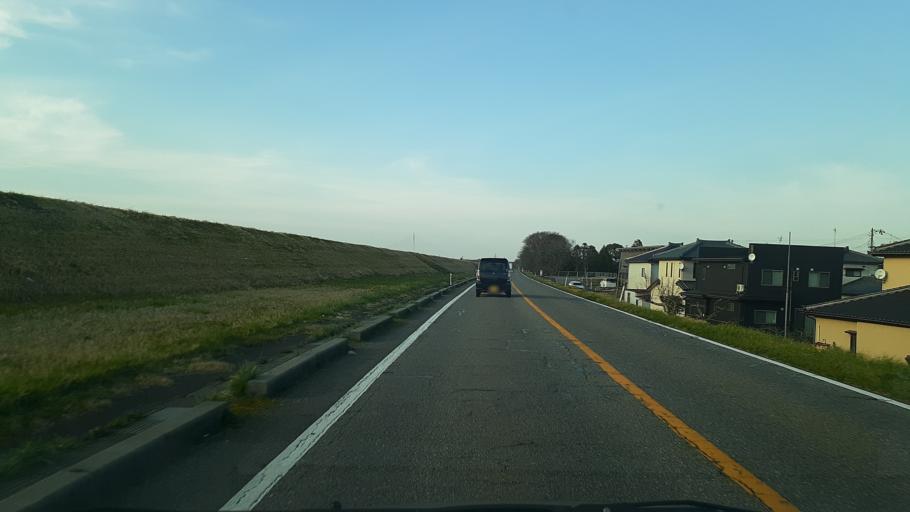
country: JP
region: Niigata
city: Niigata-shi
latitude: 37.8584
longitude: 139.0246
